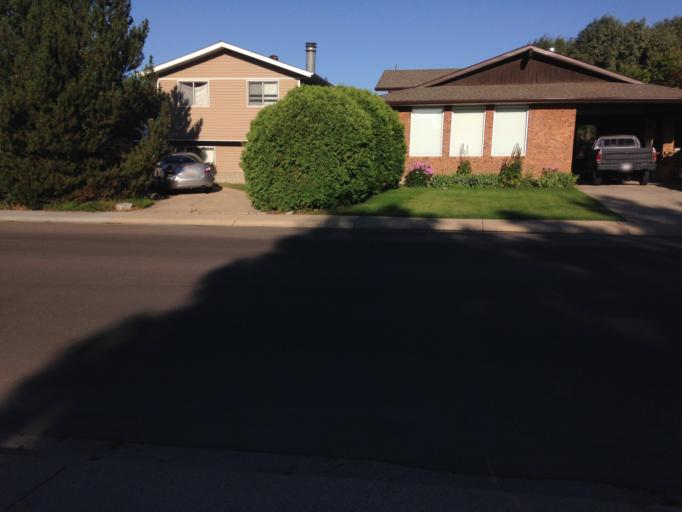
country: CA
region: Alberta
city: Medicine Hat
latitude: 50.0023
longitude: -110.6251
